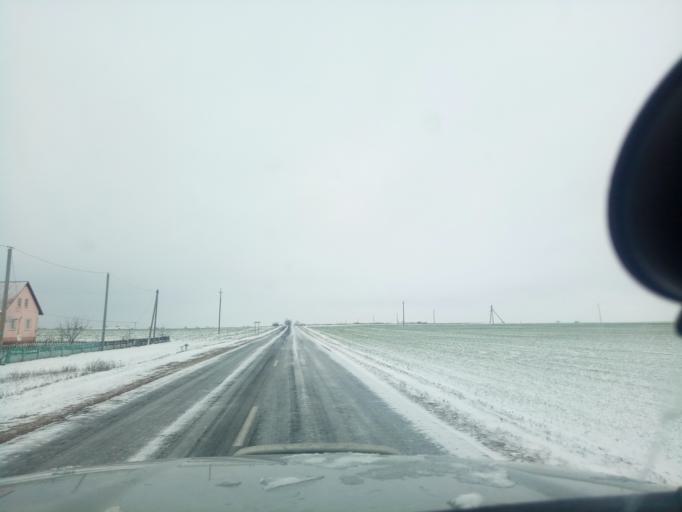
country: BY
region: Minsk
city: Klyetsk
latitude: 53.0512
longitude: 26.7572
